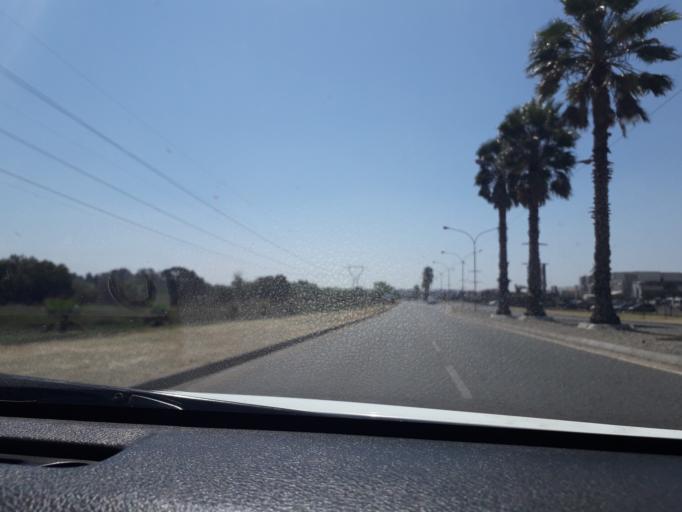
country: ZA
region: Gauteng
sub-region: City of Johannesburg Metropolitan Municipality
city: Modderfontein
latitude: -26.1079
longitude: 28.2222
